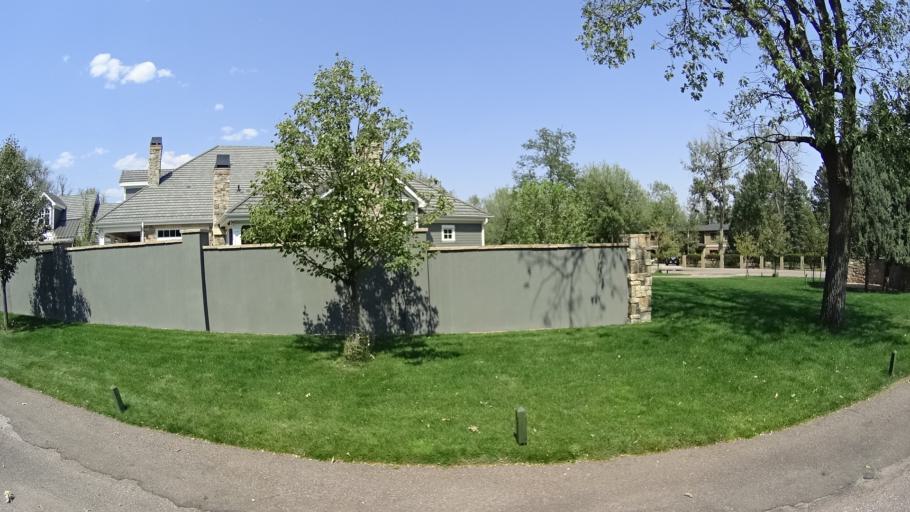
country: US
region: Colorado
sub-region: El Paso County
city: Colorado Springs
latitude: 38.7906
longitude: -104.8473
